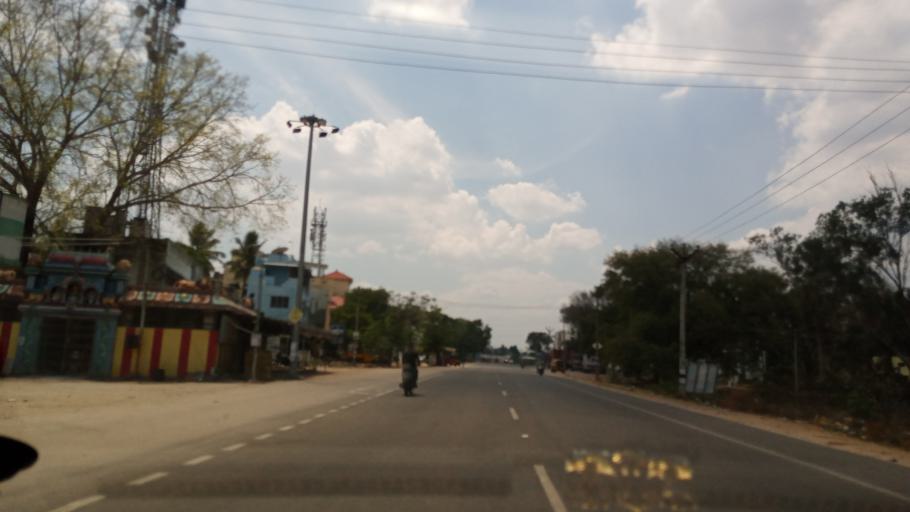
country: IN
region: Tamil Nadu
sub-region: Vellore
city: Walajapet
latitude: 12.9218
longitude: 79.3774
